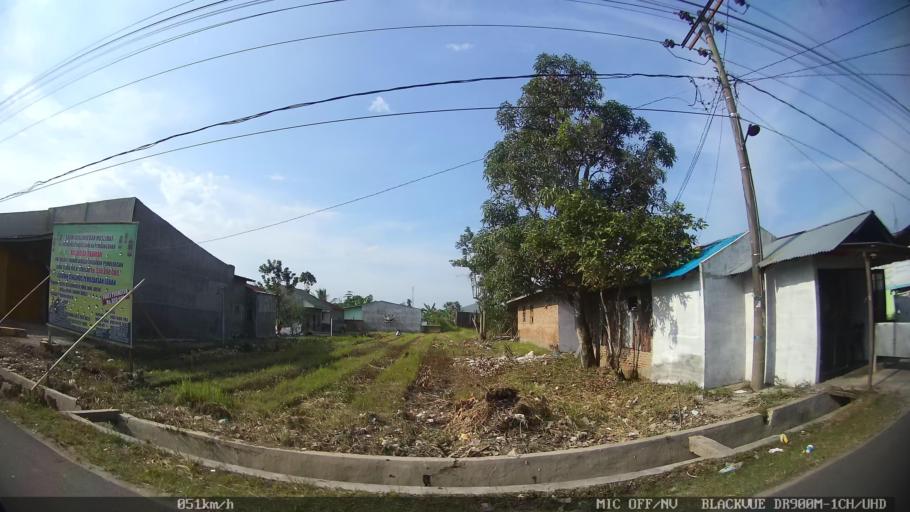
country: ID
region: North Sumatra
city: Percut
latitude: 3.5939
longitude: 98.7745
